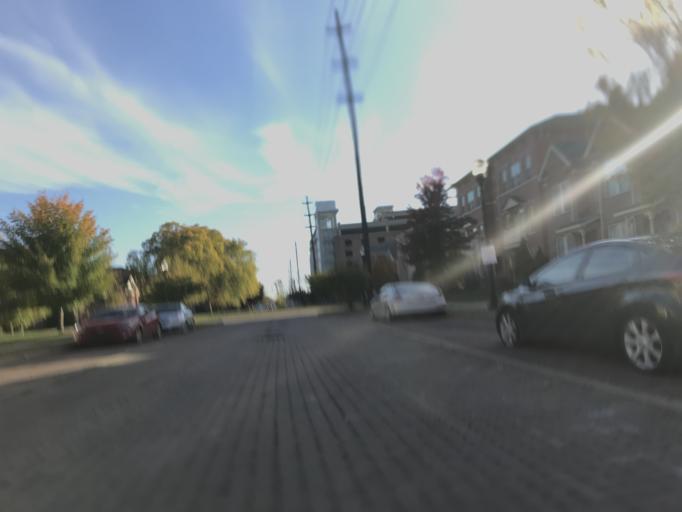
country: US
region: Kentucky
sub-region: Jefferson County
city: Louisville
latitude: 38.2506
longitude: -85.7406
